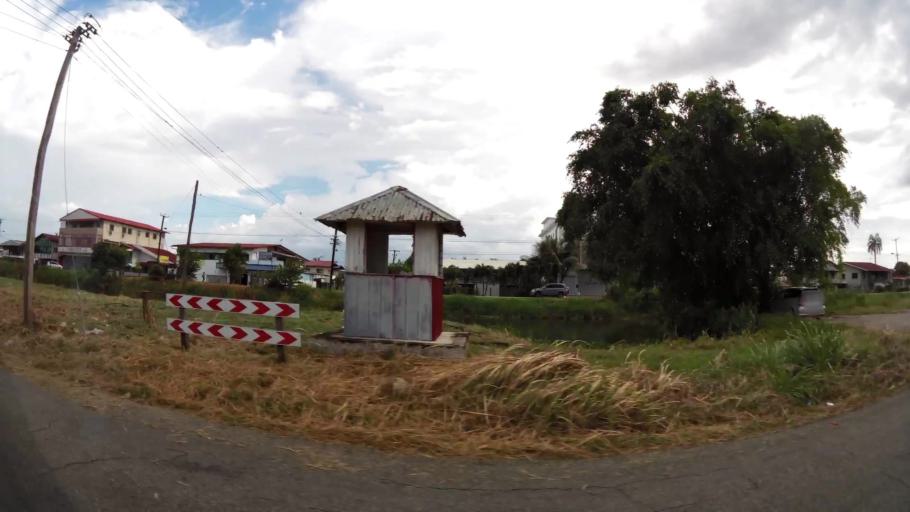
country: SR
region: Paramaribo
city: Paramaribo
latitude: 5.8391
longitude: -55.1369
